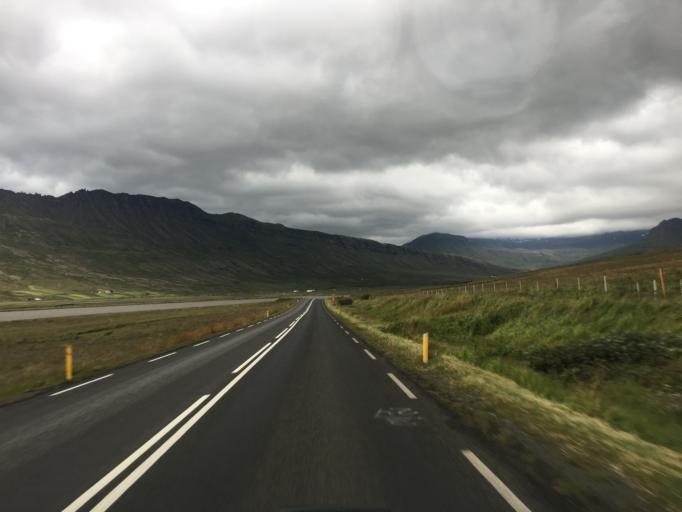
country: IS
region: East
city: Neskaupstadur
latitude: 65.1373
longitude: -13.7471
